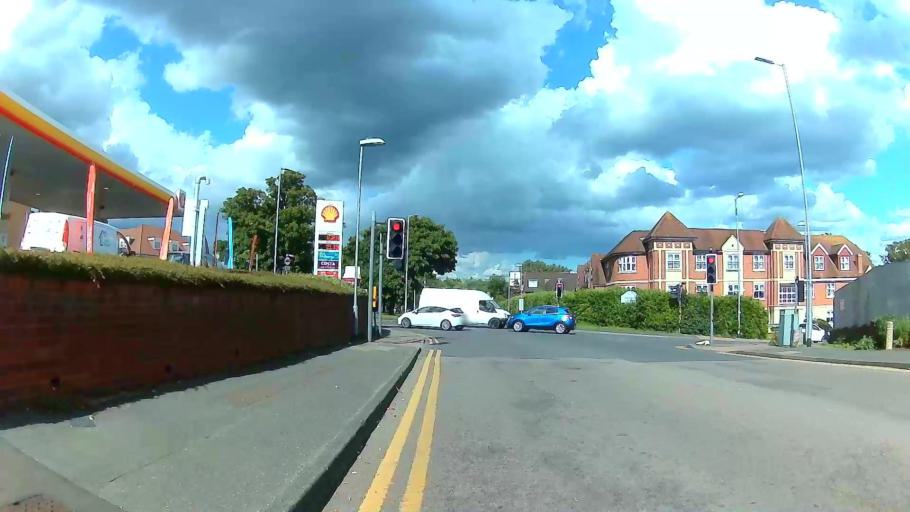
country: GB
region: England
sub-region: Essex
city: Grange Hill
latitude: 51.6105
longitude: 0.0813
